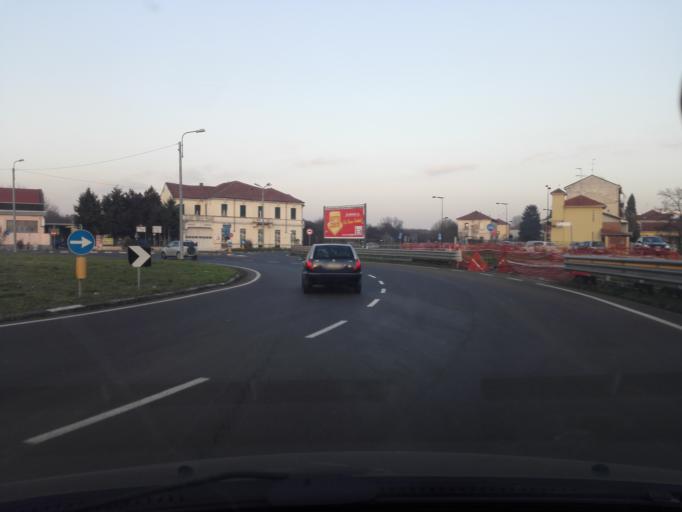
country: IT
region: Piedmont
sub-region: Provincia di Alessandria
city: Alessandria
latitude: 44.9168
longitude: 8.6009
